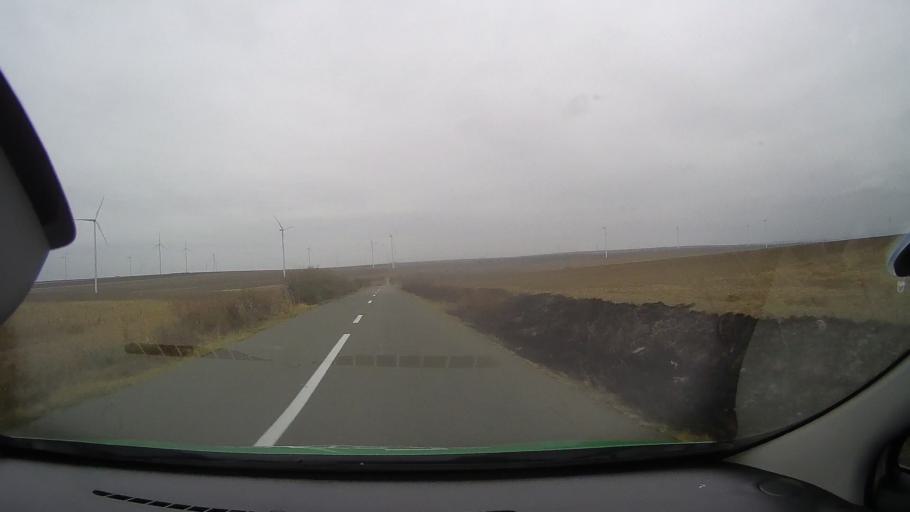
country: RO
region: Constanta
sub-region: Comuna Pantelimon
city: Pantelimon
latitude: 44.5107
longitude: 28.3387
